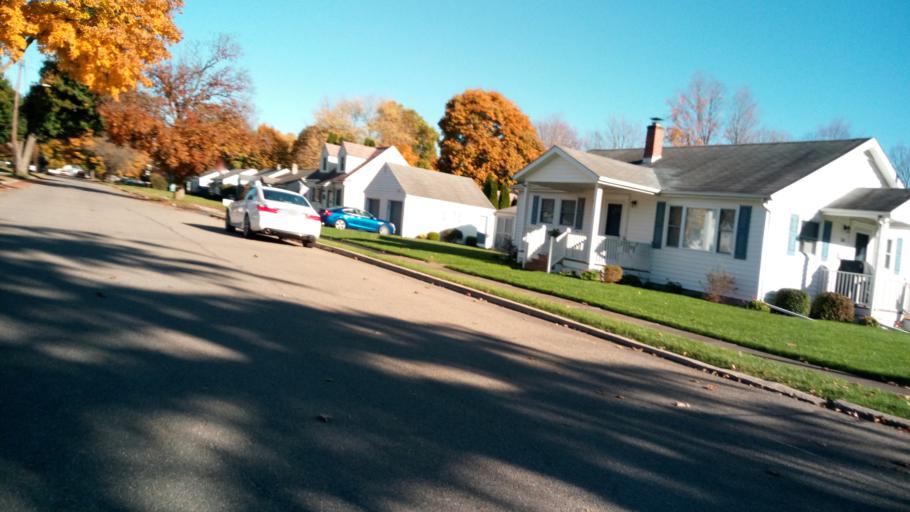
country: US
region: New York
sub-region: Chemung County
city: Southport
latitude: 42.0669
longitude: -76.8117
